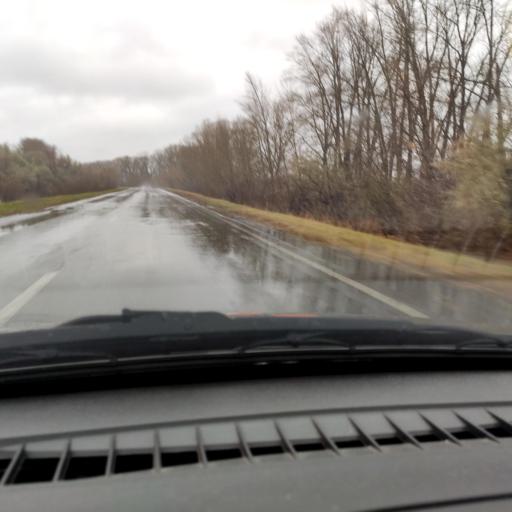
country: RU
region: Samara
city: Tol'yatti
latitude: 53.6556
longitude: 49.2891
